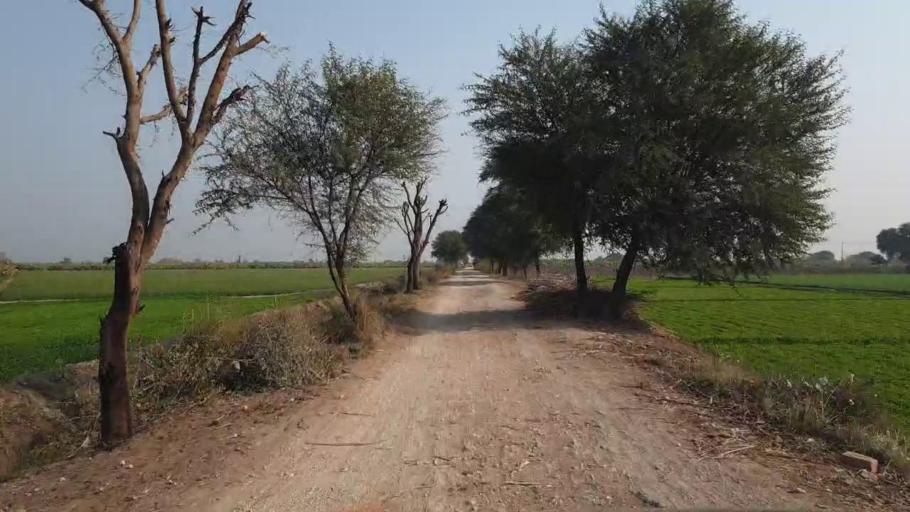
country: PK
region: Sindh
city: Hala
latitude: 25.8871
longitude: 68.4453
